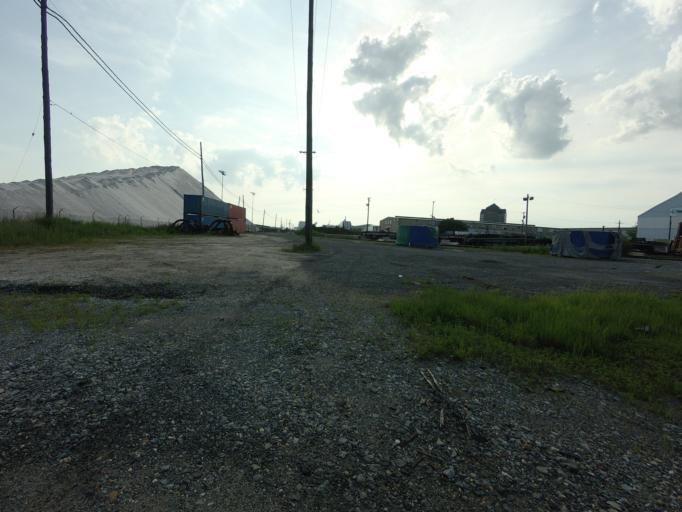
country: US
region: Maryland
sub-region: Baltimore County
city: Dundalk
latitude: 39.2715
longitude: -76.5605
